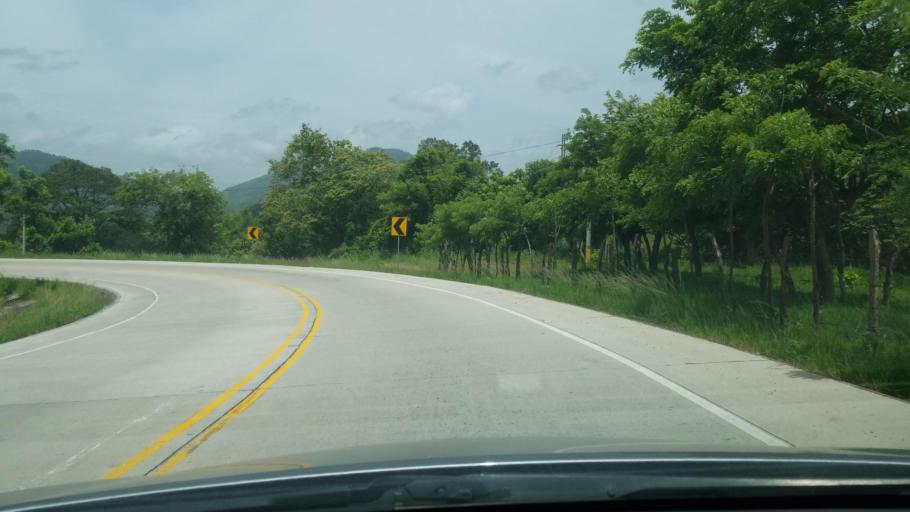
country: HN
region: Copan
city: Quezailica
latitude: 14.9008
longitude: -88.7567
